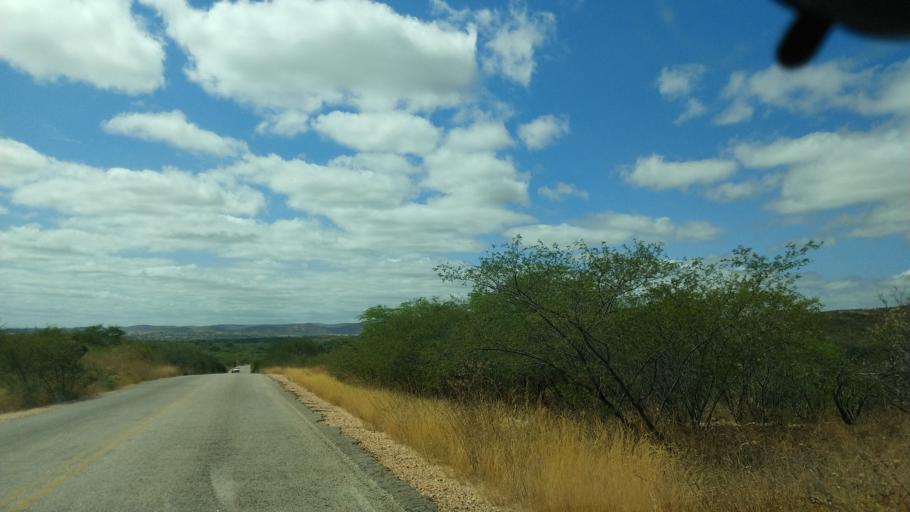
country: BR
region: Rio Grande do Norte
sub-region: Currais Novos
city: Currais Novos
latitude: -6.2609
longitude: -36.5733
